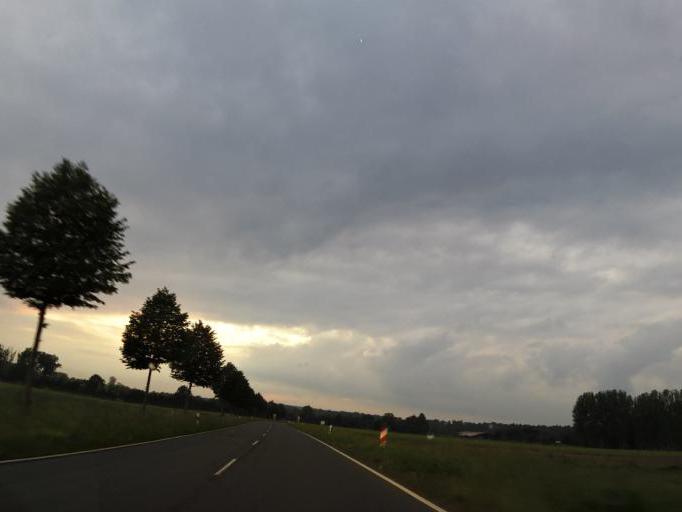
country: DE
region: Hesse
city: Dieburg
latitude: 49.9034
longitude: 8.8212
